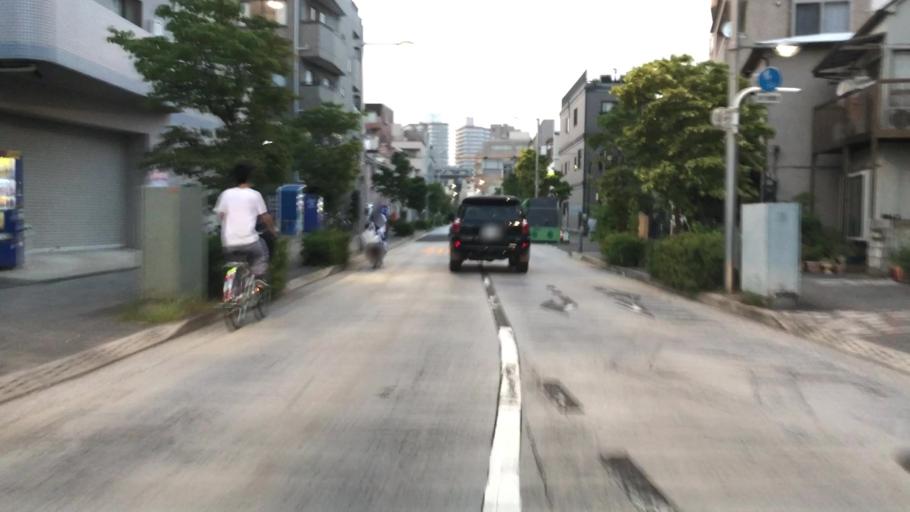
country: JP
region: Saitama
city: Soka
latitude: 35.7449
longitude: 139.7757
